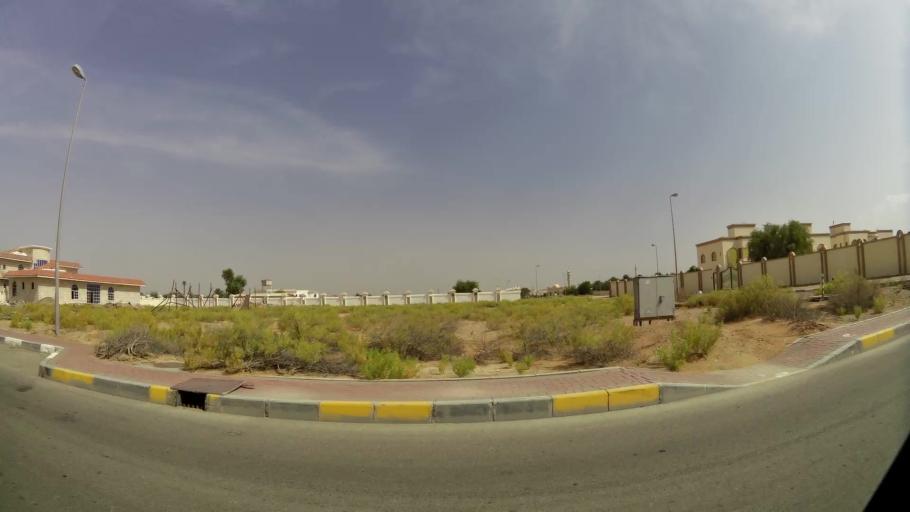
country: AE
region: Abu Dhabi
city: Al Ain
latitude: 24.1585
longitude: 55.6752
